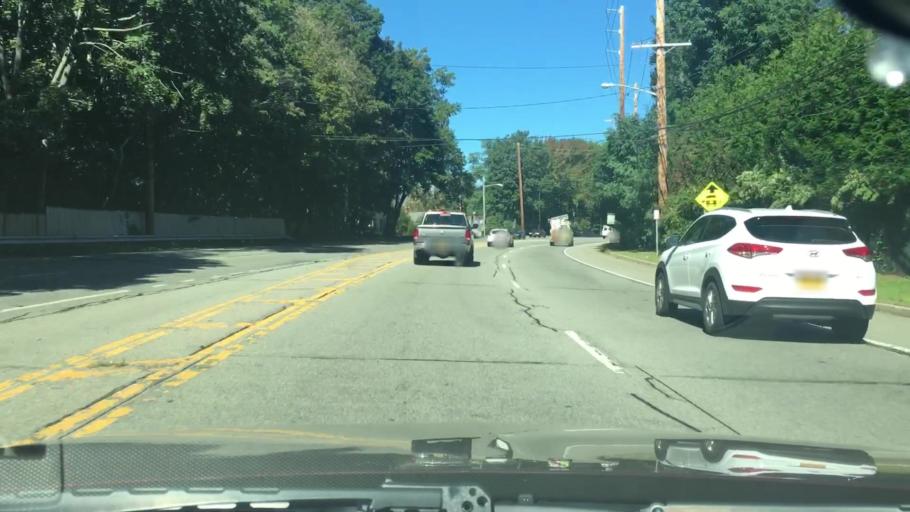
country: US
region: New York
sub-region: Nassau County
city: Flower Hill
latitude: 40.8138
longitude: -73.6800
